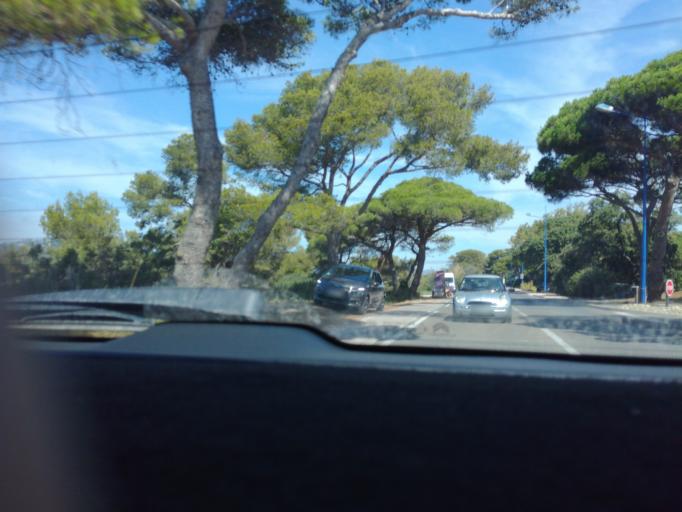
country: FR
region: Provence-Alpes-Cote d'Azur
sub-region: Departement du Var
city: Hyeres
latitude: 43.0588
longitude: 6.1469
